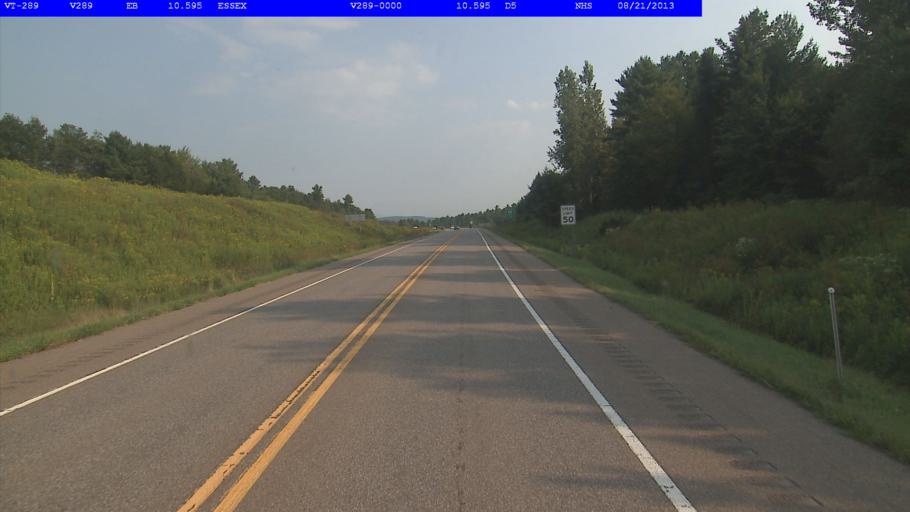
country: US
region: Vermont
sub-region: Chittenden County
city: Essex Junction
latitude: 44.4985
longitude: -73.0700
